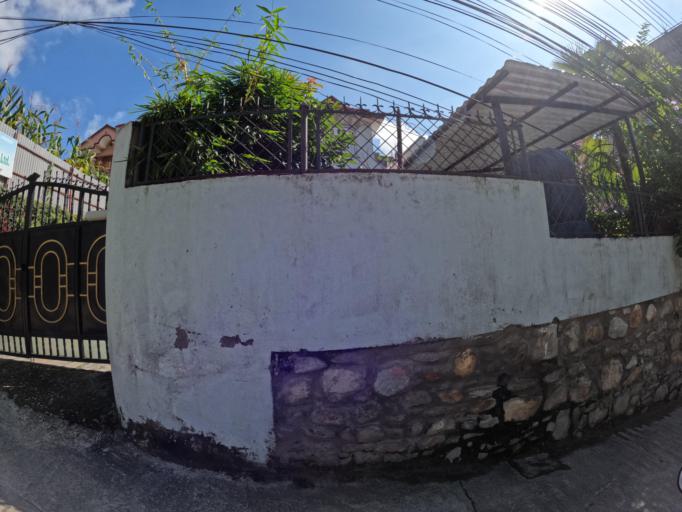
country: NP
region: Central Region
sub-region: Bagmati Zone
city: Kathmandu
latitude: 27.7463
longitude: 85.3345
